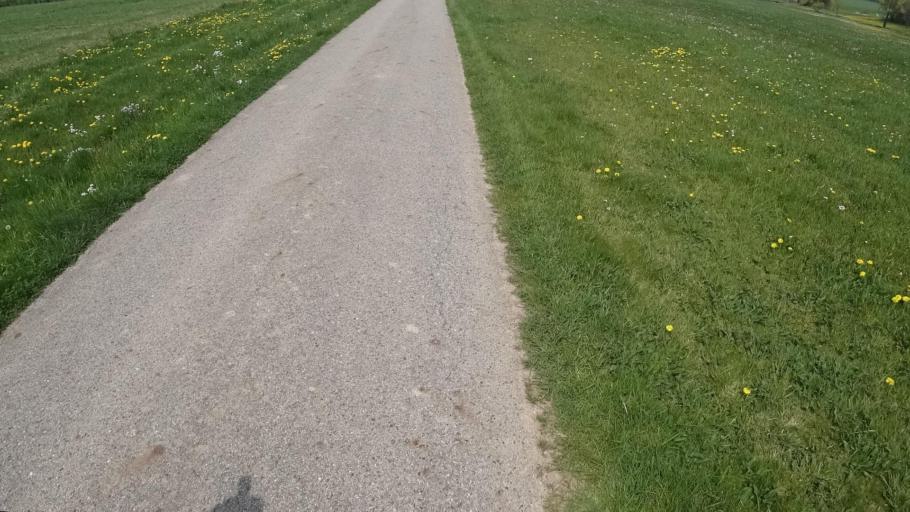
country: DE
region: Rheinland-Pfalz
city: Bubach
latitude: 50.0698
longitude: 7.5525
